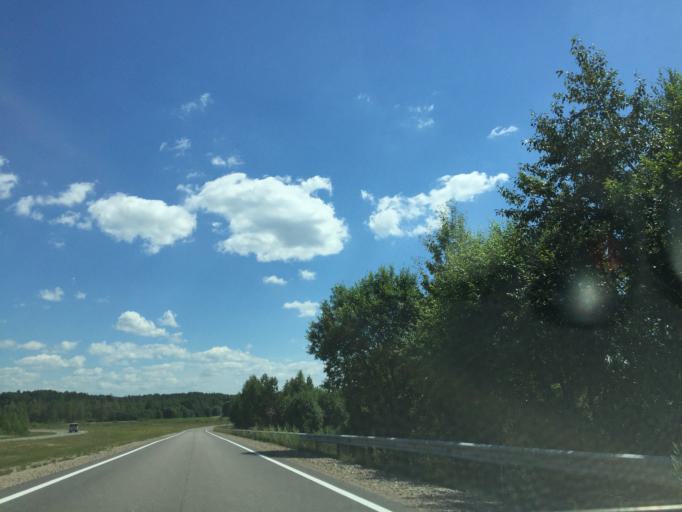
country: LV
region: Rezekne
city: Rezekne
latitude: 56.4793
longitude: 27.2936
